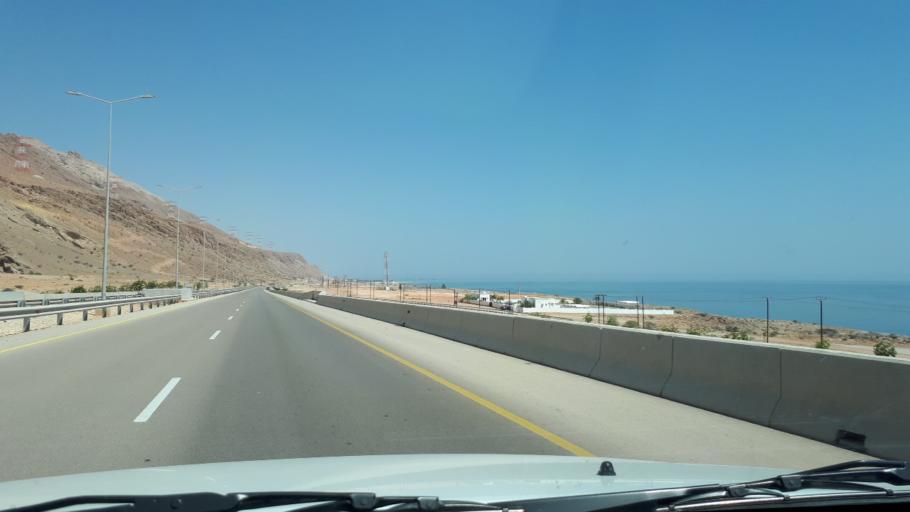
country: OM
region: Ash Sharqiyah
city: Sur
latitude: 22.7869
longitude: 59.2773
